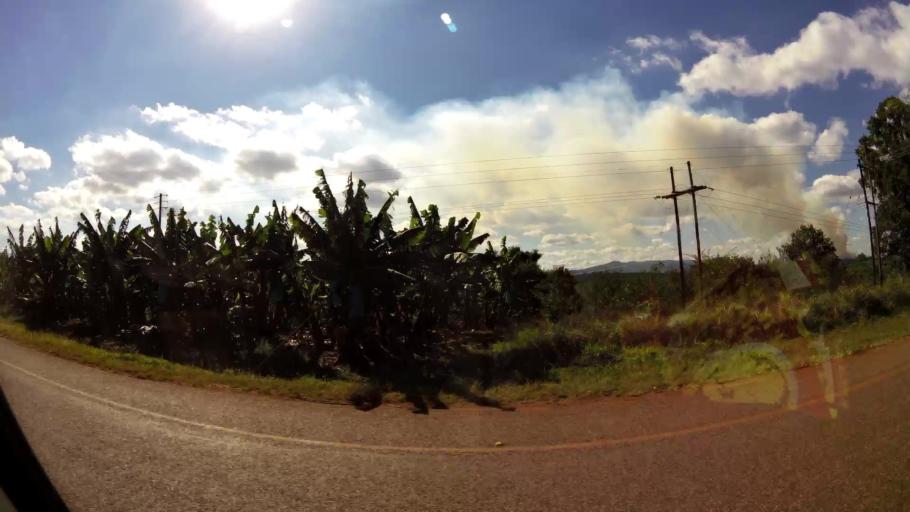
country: ZA
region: Limpopo
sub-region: Mopani District Municipality
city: Tzaneen
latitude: -23.8047
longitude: 30.1120
